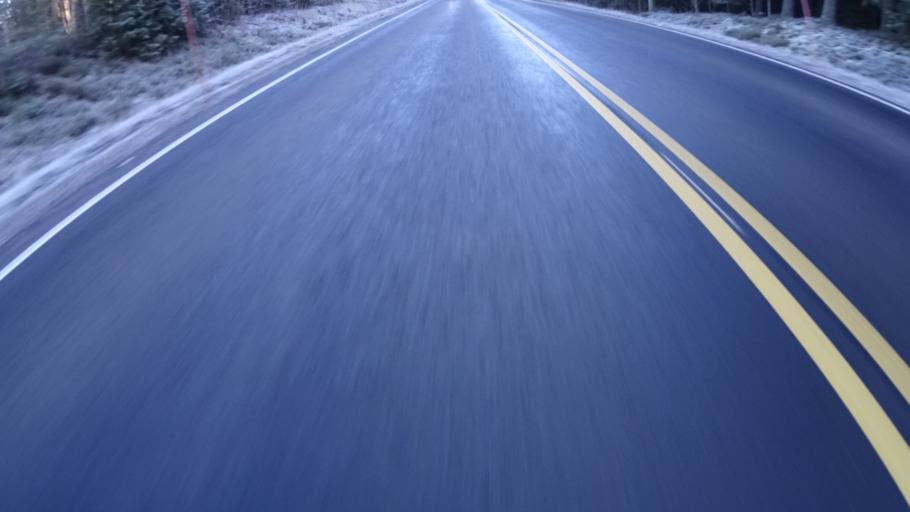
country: FI
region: Uusimaa
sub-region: Helsinki
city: Vihti
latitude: 60.5132
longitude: 24.4402
